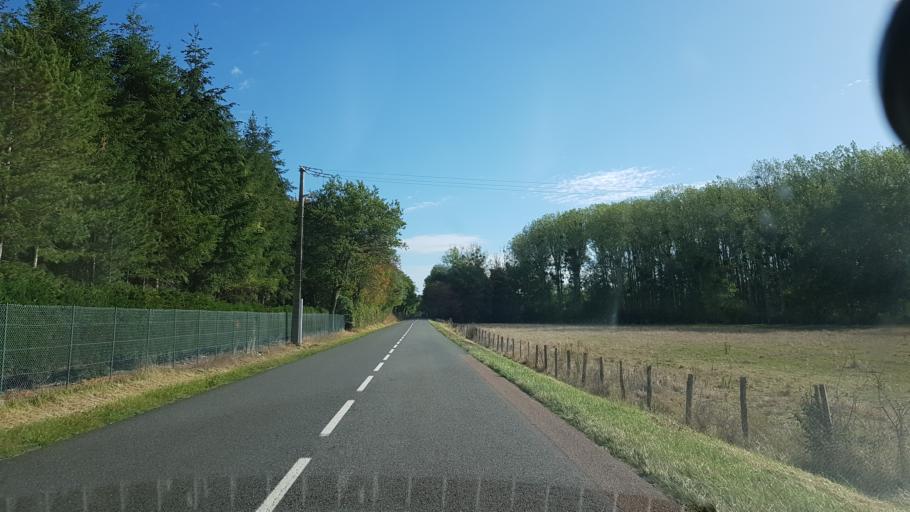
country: FR
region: Bourgogne
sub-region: Departement de la Nievre
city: Neuvy-sur-Loire
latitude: 47.5344
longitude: 2.9176
